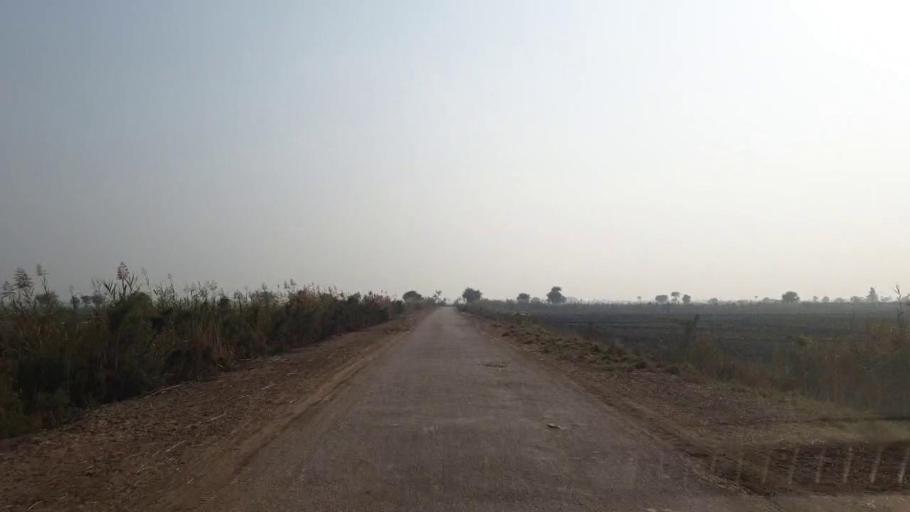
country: PK
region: Sindh
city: Shahdadpur
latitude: 25.9687
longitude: 68.5154
